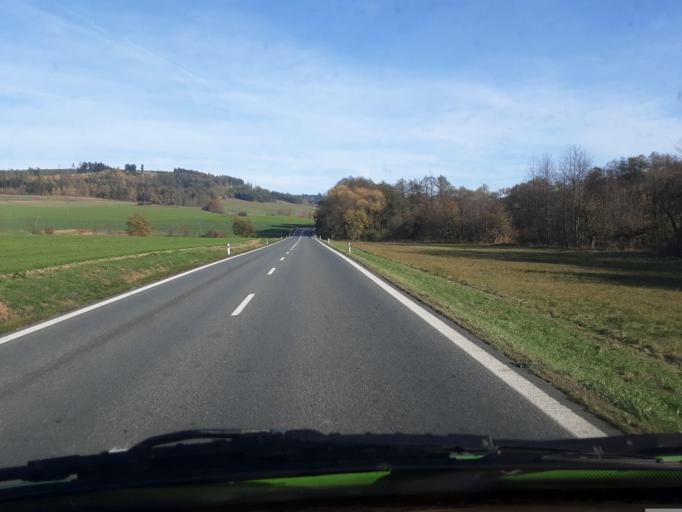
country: CZ
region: Plzensky
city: Klatovy
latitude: 49.3602
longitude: 13.3729
